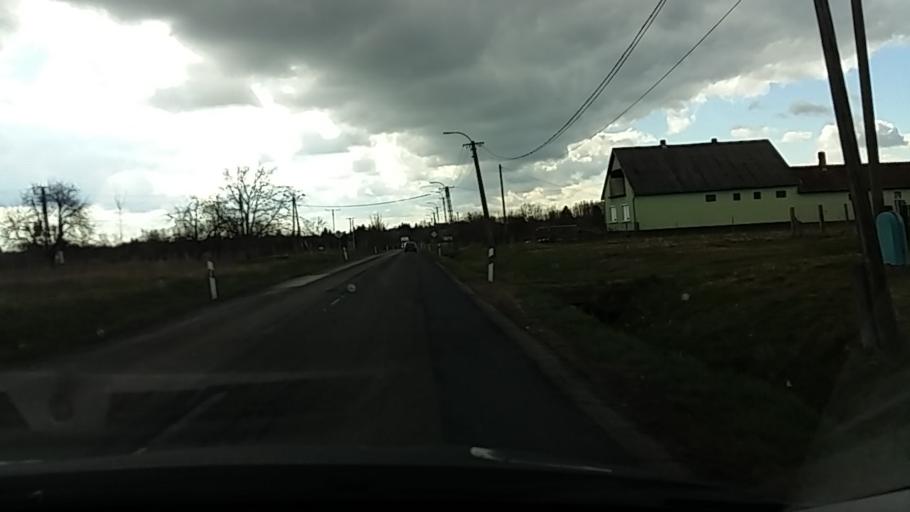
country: HU
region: Somogy
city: Bohonye
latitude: 46.4192
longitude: 17.3821
